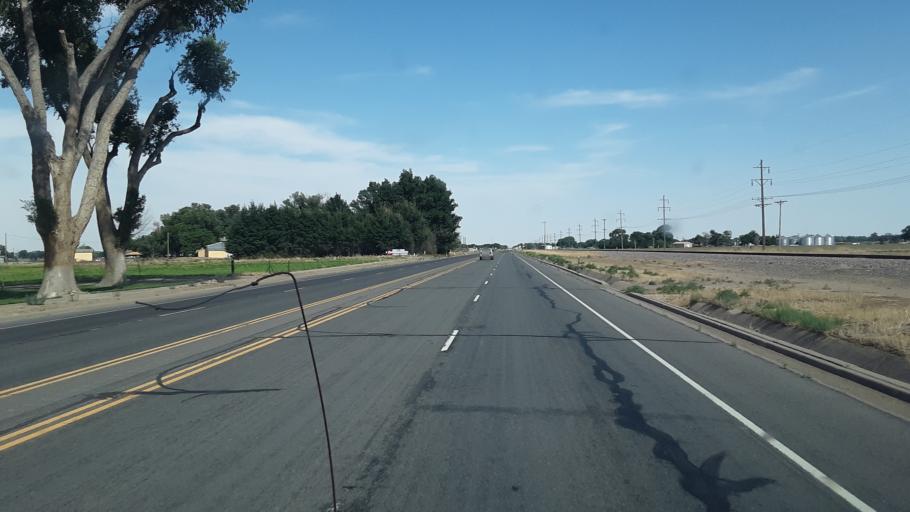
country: US
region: Colorado
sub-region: Otero County
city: Rocky Ford
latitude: 38.0672
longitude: -103.7551
